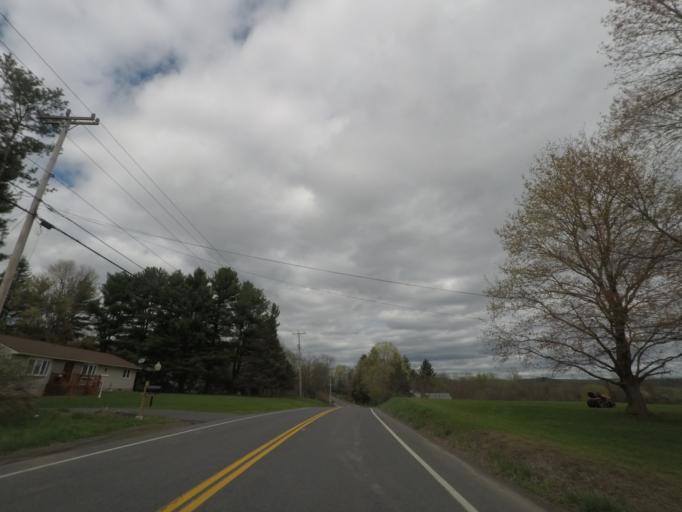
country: US
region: New York
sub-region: Columbia County
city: Philmont
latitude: 42.2796
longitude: -73.6592
